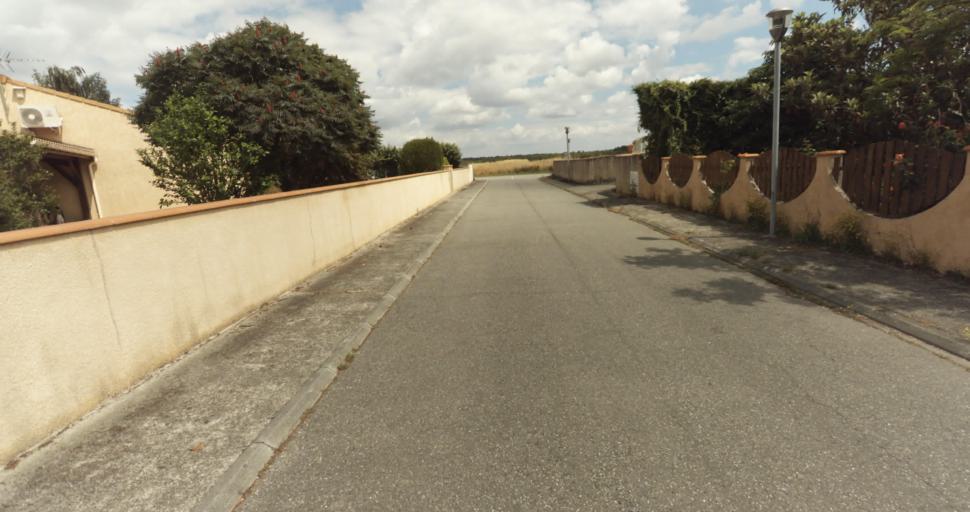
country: FR
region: Midi-Pyrenees
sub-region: Departement de la Haute-Garonne
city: Fontenilles
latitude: 43.5572
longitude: 1.1838
